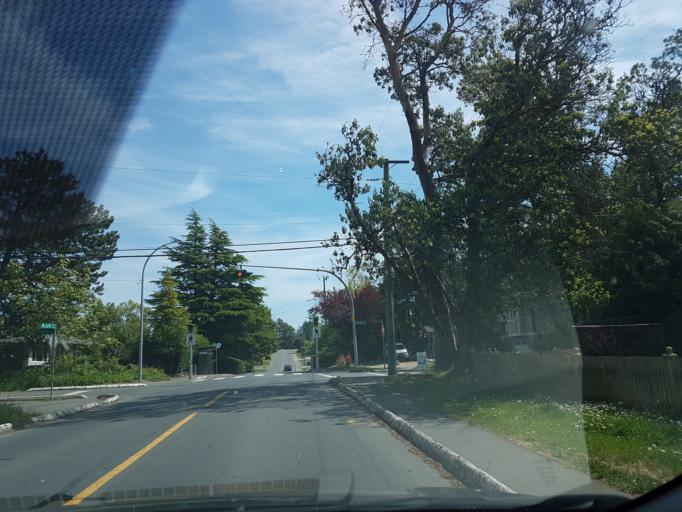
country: CA
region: British Columbia
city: Oak Bay
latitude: 48.4908
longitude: -123.3225
